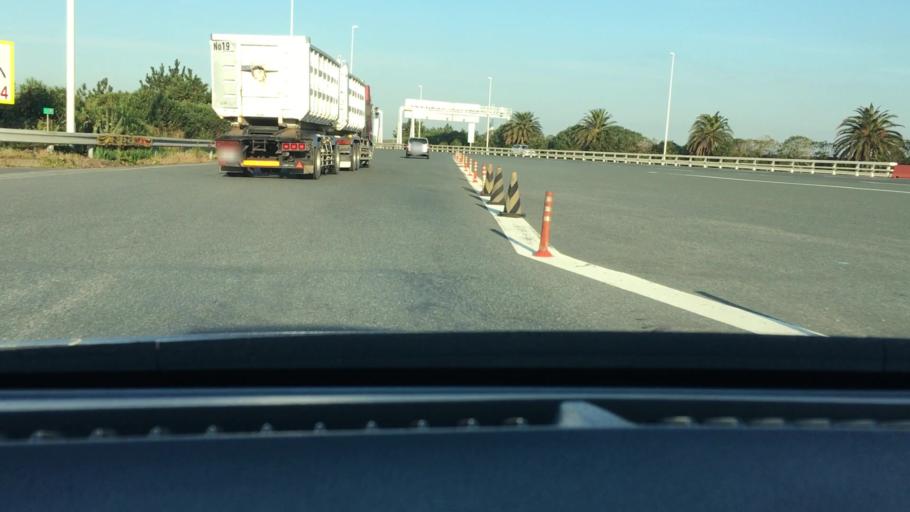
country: JP
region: Chiba
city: Kisarazu
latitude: 35.4357
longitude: 139.9179
